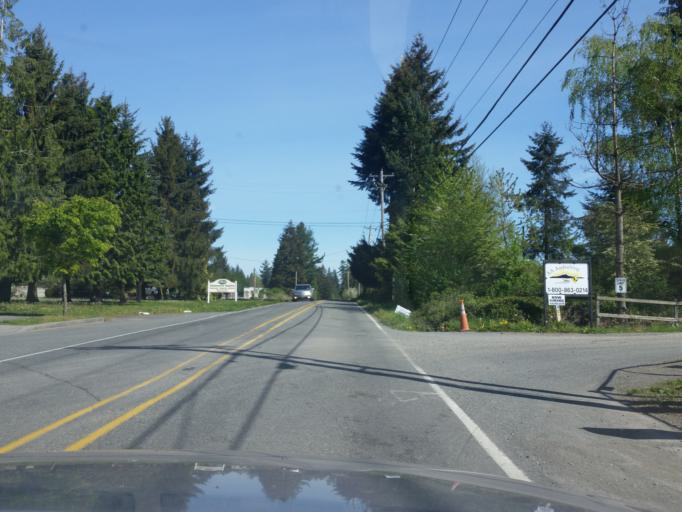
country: US
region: Washington
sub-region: Snohomish County
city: Maltby
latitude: 47.8147
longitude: -122.1100
